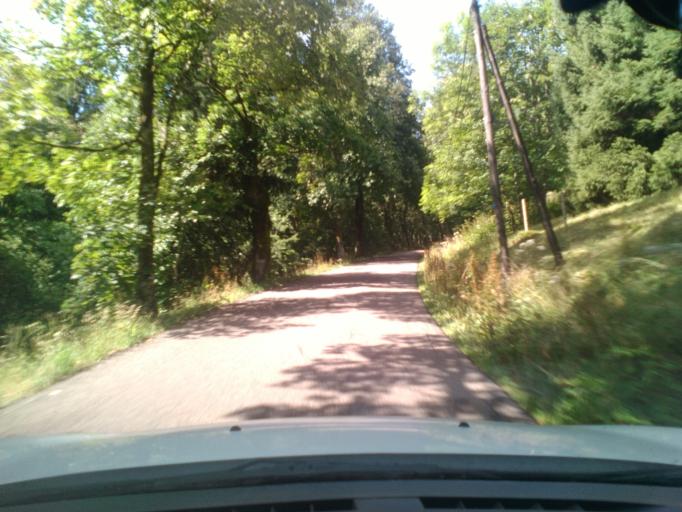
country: FR
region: Lorraine
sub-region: Departement des Vosges
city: Gerardmer
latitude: 48.0494
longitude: 6.8439
